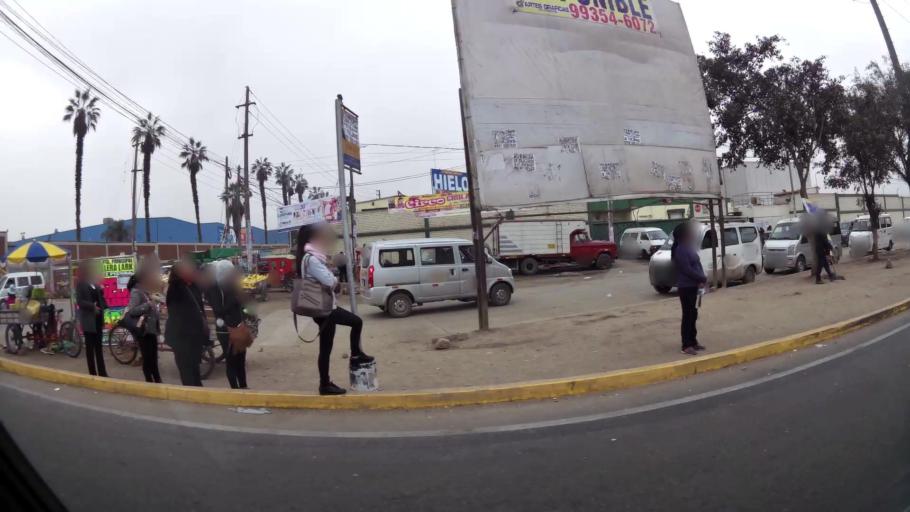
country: PE
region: Lima
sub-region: Lima
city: Carabayllo
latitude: -11.8677
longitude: -77.0723
